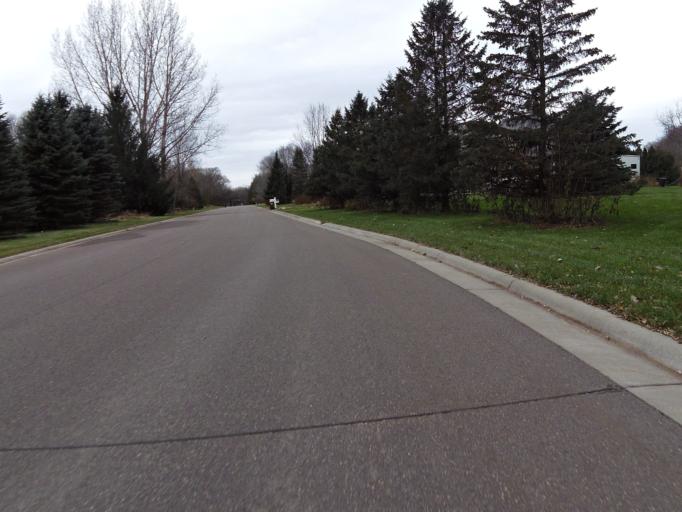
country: US
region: Minnesota
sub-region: Washington County
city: Lake Elmo
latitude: 44.9848
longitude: -92.8746
